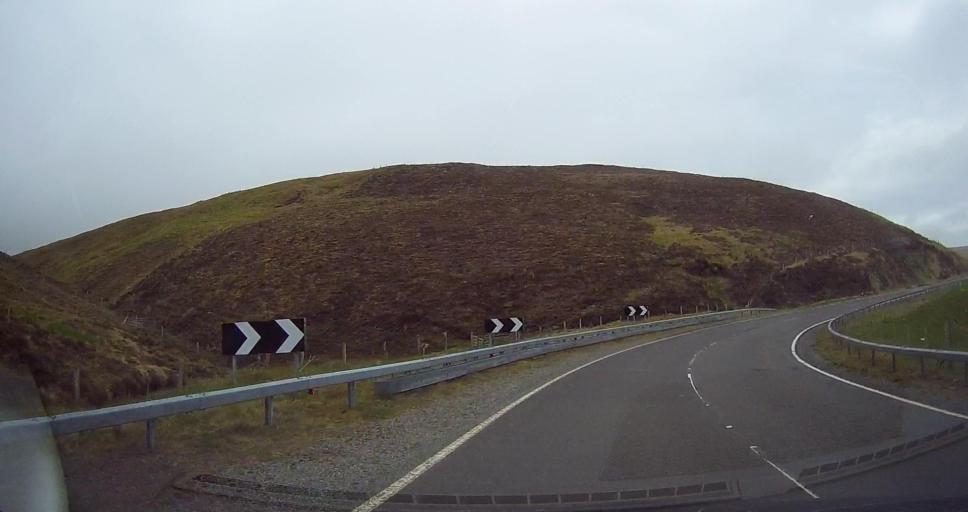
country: GB
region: Scotland
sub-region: Shetland Islands
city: Sandwick
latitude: 59.9903
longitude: -1.2839
